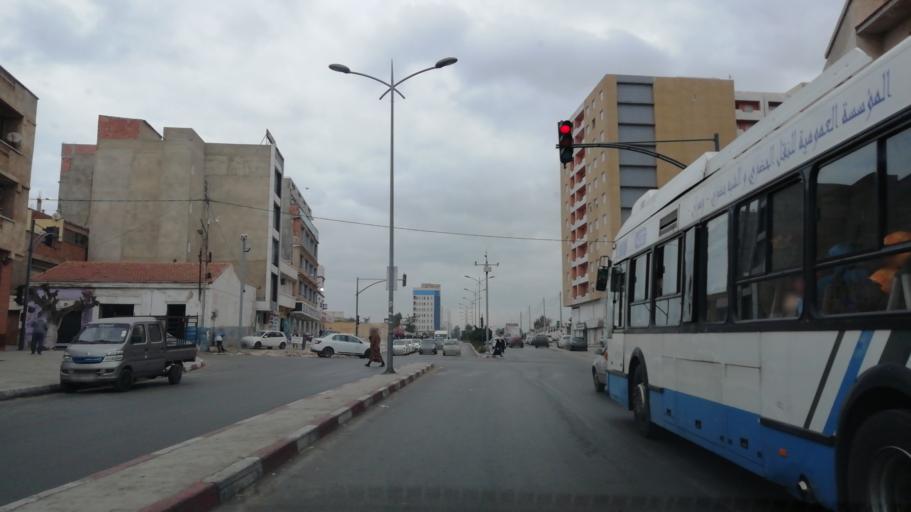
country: DZ
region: Oran
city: Oran
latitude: 35.6884
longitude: -0.6230
